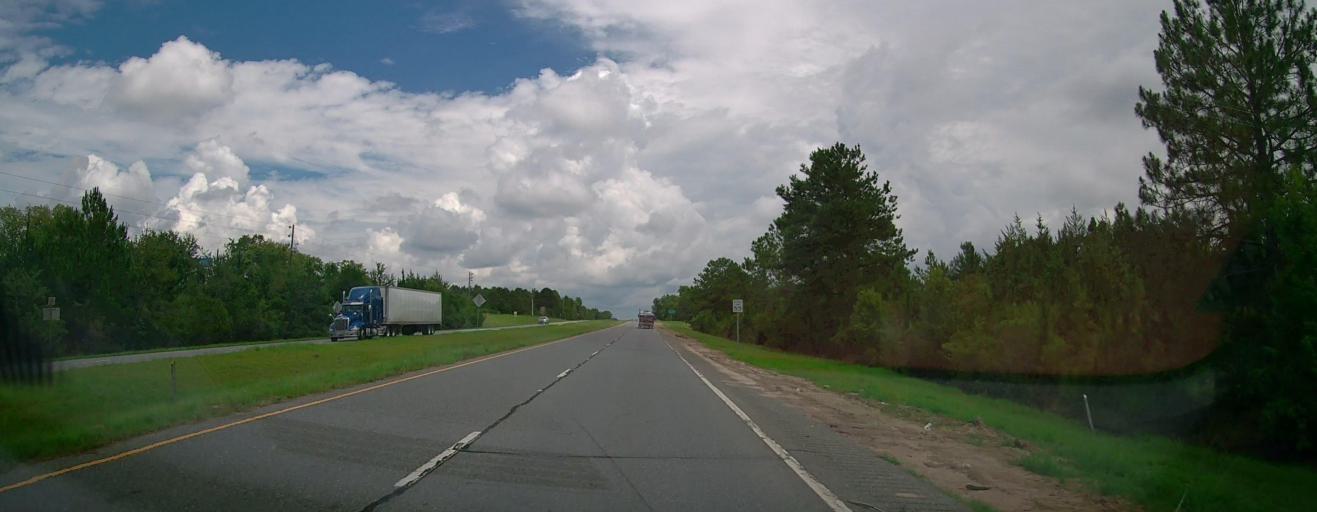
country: US
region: Georgia
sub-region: Dodge County
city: Eastman
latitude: 32.1776
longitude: -83.1805
